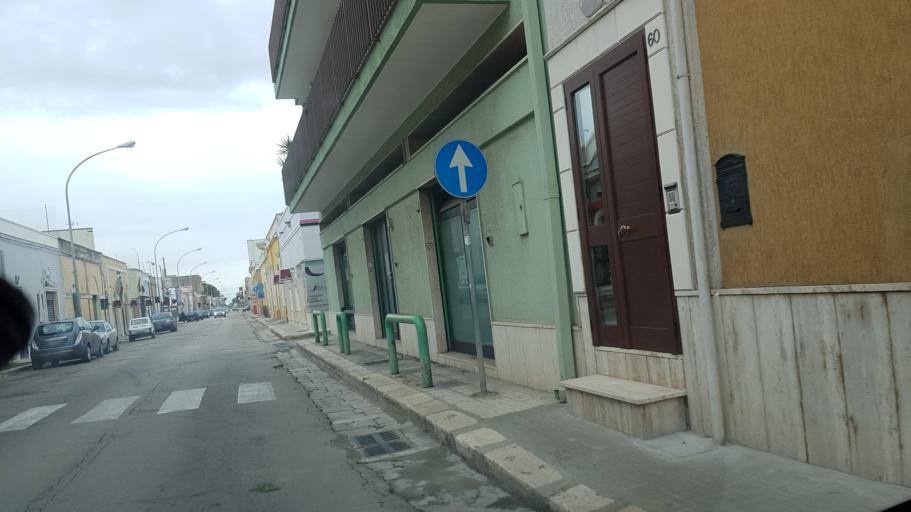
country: IT
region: Apulia
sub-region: Provincia di Lecce
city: Squinzano
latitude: 40.4353
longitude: 18.0405
